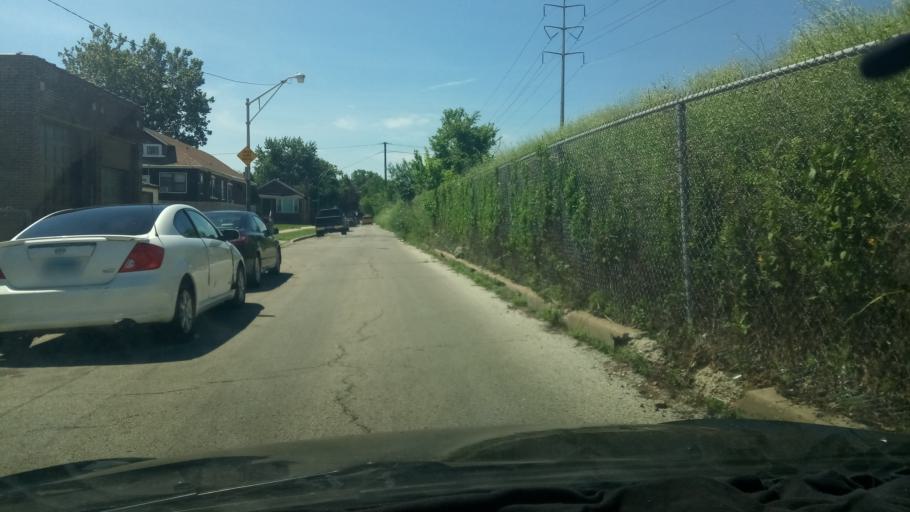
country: US
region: Illinois
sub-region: Cook County
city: Hometown
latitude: 41.7731
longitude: -87.7133
